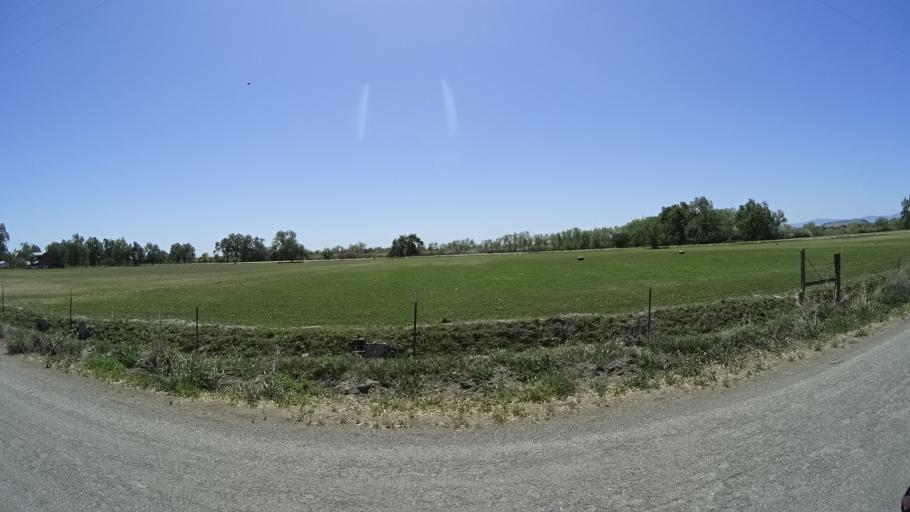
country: US
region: California
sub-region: Glenn County
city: Orland
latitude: 39.7956
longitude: -122.2473
